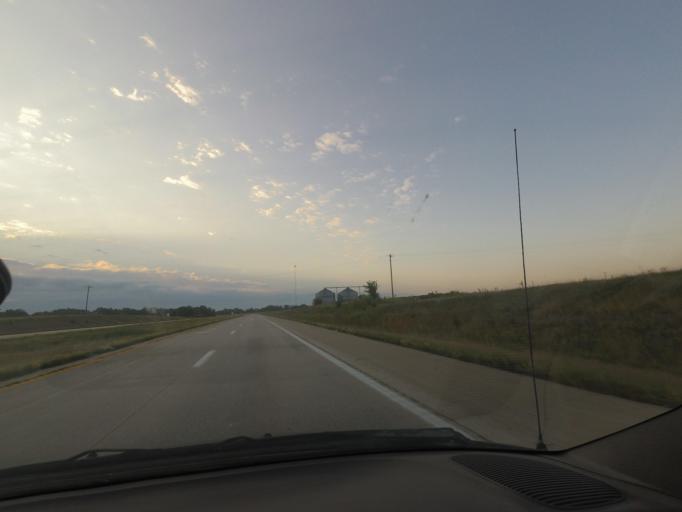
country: US
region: Missouri
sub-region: Shelby County
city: Shelbina
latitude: 39.7474
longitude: -92.2469
